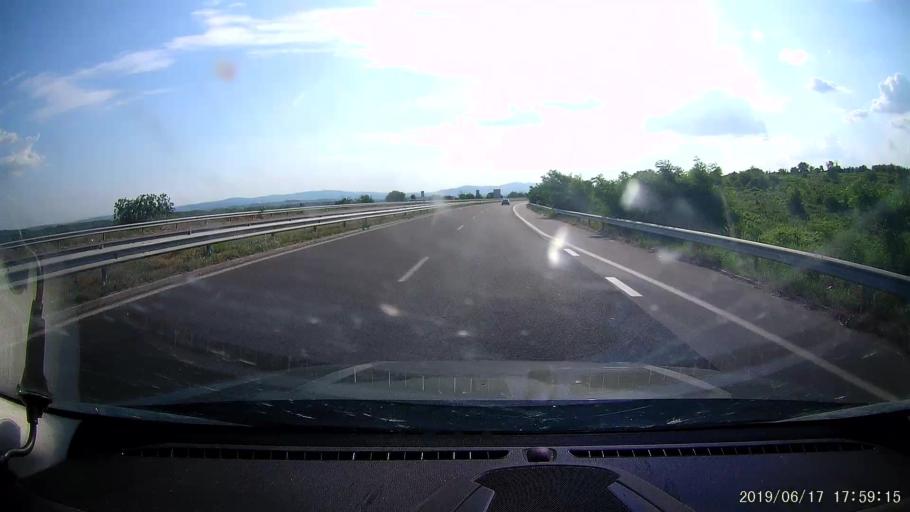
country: BG
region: Khaskovo
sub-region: Obshtina Svilengrad
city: Svilengrad
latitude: 41.7246
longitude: 26.3027
